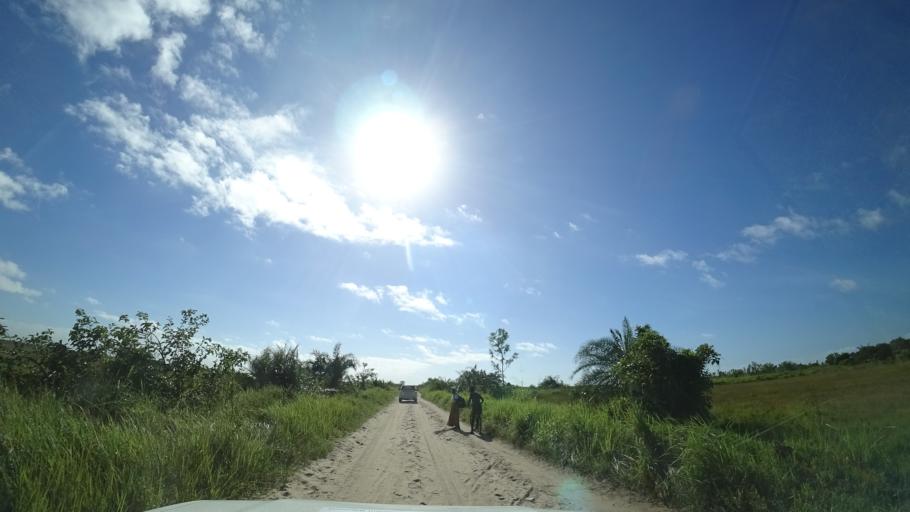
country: MZ
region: Sofala
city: Beira
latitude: -19.7127
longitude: 35.0132
